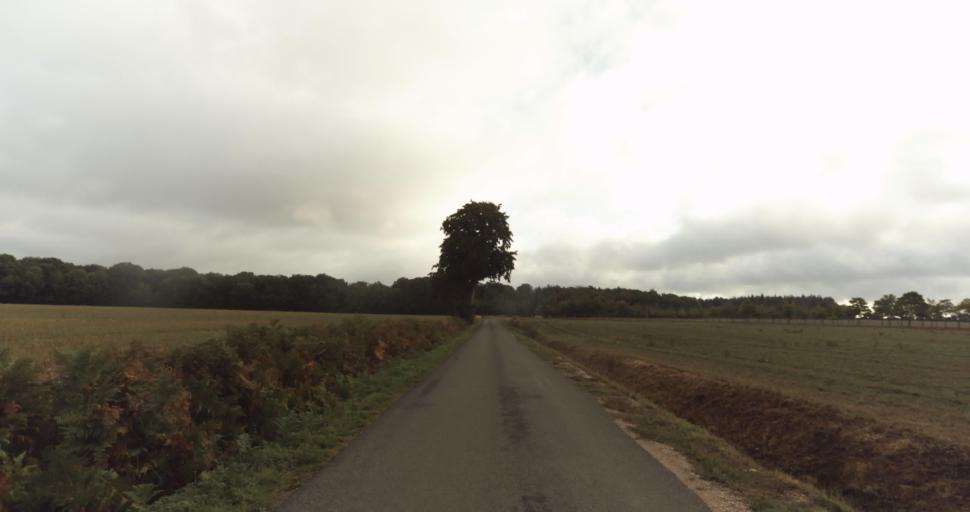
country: FR
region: Lower Normandy
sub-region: Departement de l'Orne
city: Vimoutiers
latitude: 48.9097
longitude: 0.2309
